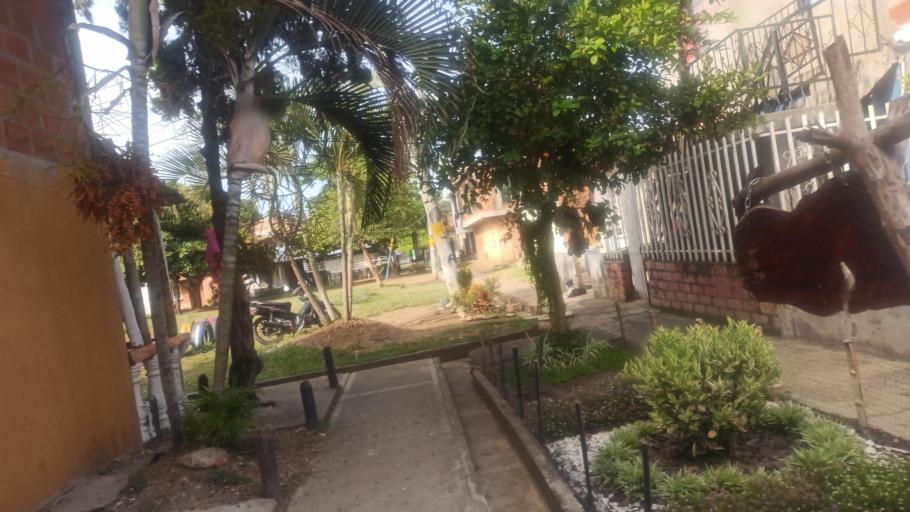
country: CO
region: Valle del Cauca
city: Jamundi
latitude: 3.2400
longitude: -76.5097
